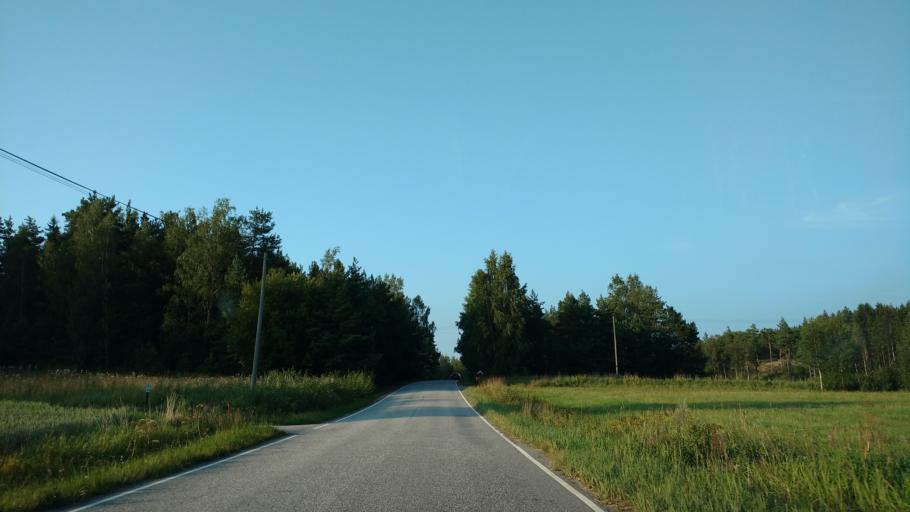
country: FI
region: Varsinais-Suomi
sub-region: Aboland-Turunmaa
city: Dragsfjaerd
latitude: 60.0420
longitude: 22.4463
